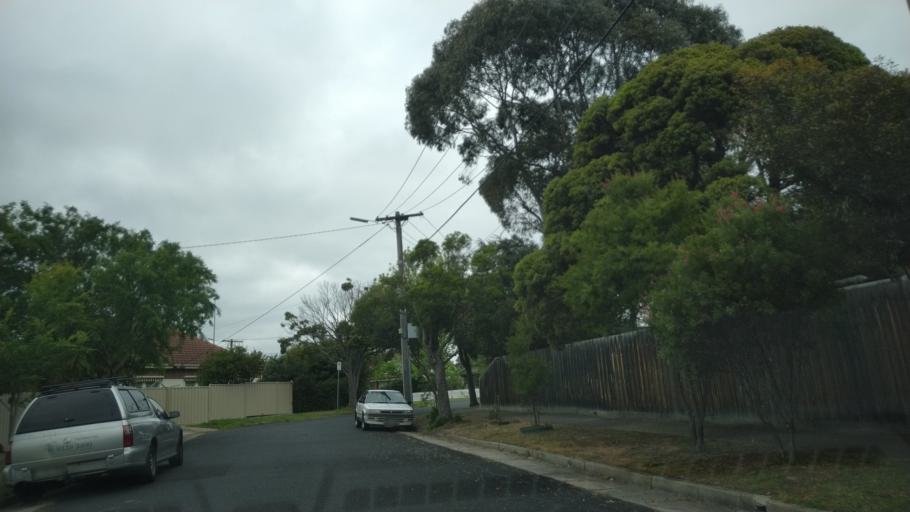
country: AU
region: Victoria
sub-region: Glen Eira
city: Murrumbeena
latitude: -37.8954
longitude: 145.0720
